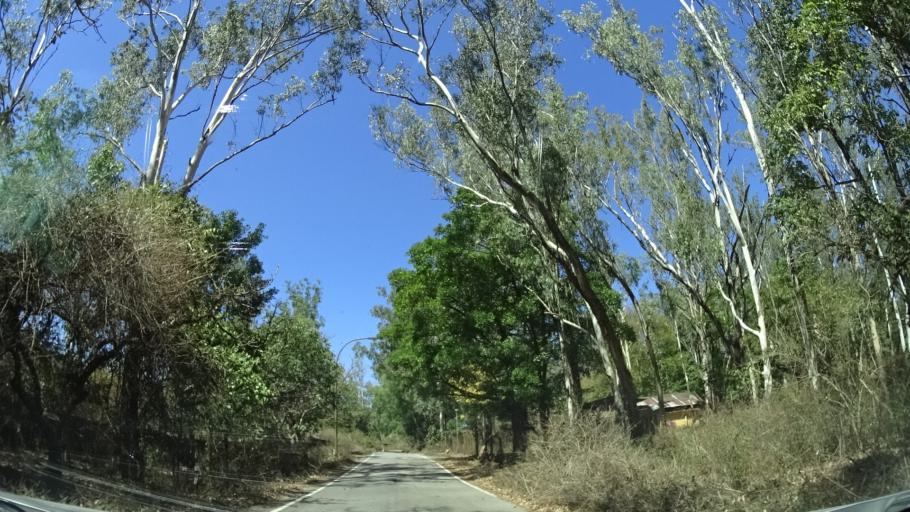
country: IN
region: Karnataka
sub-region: Chikmagalur
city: Sringeri
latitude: 13.2133
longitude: 75.2486
